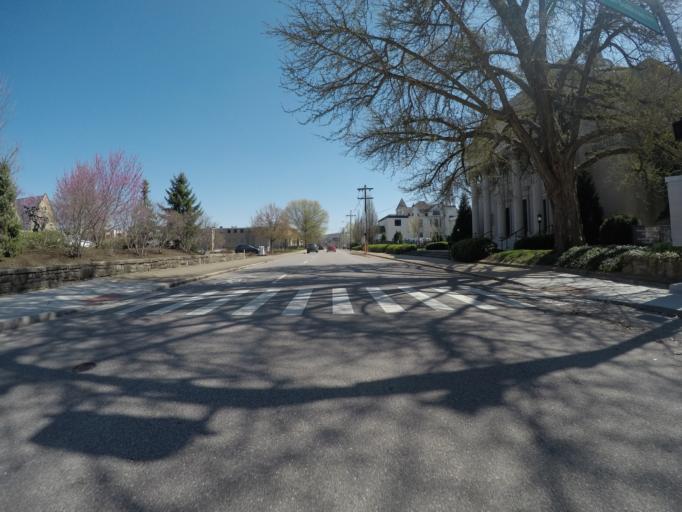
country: US
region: West Virginia
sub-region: Kanawha County
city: Charleston
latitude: 38.3468
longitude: -81.6330
